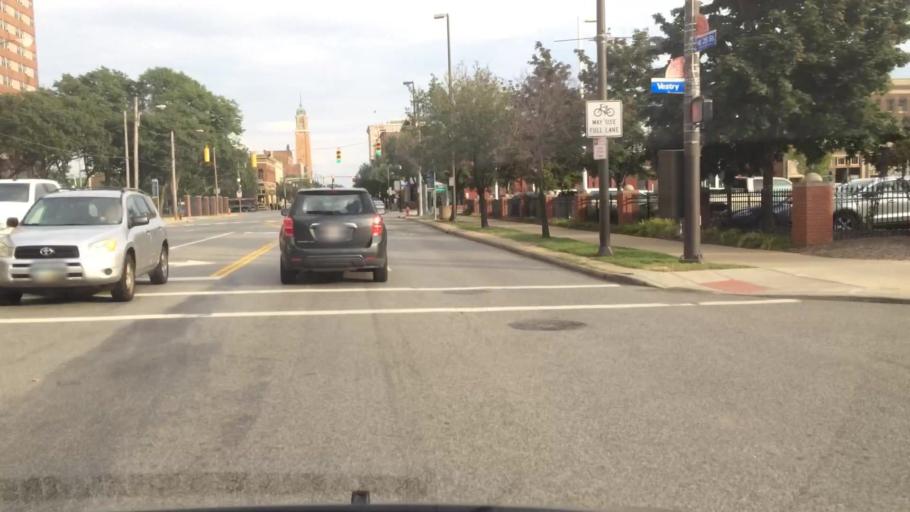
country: US
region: Ohio
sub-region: Cuyahoga County
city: Cleveland
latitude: 41.4873
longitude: -81.7059
